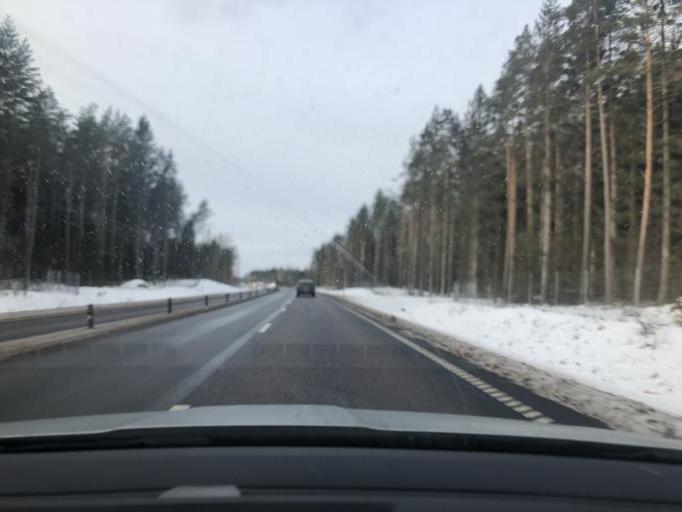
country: SE
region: OEstergoetland
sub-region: Motala Kommun
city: Borensberg
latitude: 58.5894
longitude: 15.1706
